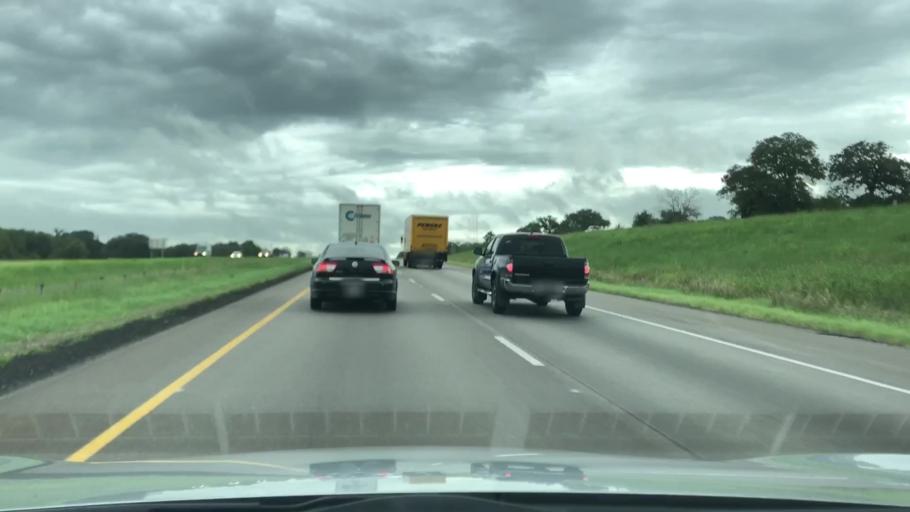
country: US
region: Texas
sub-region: Caldwell County
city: Luling
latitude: 29.6541
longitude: -97.5787
